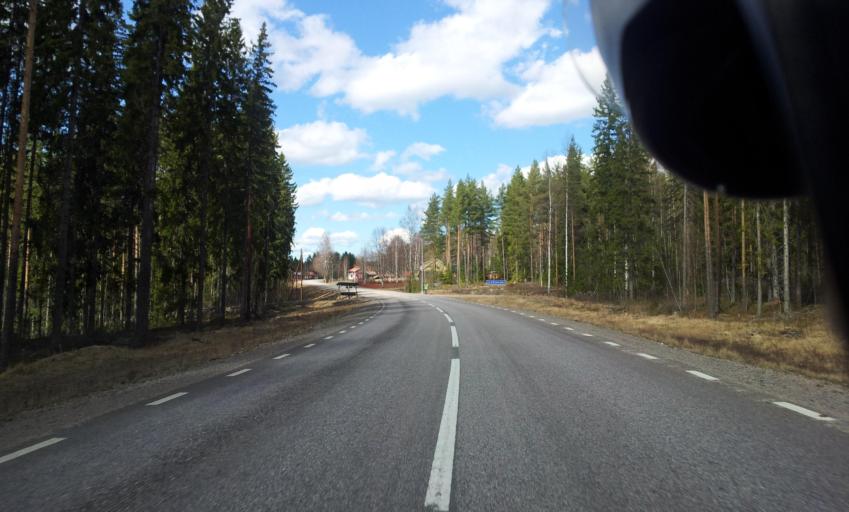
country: SE
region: Gaevleborg
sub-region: Ovanakers Kommun
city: Edsbyn
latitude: 61.2000
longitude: 15.8739
